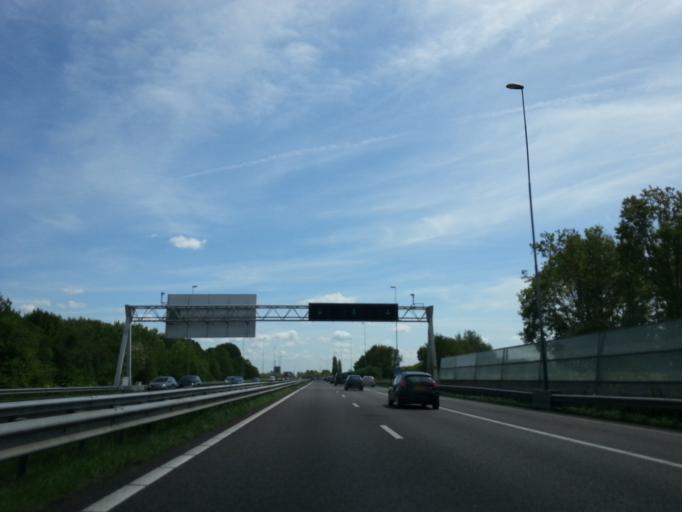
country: NL
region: North Holland
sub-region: Gemeente Velsen
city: Velsen-Zuid
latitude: 52.4305
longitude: 4.6782
